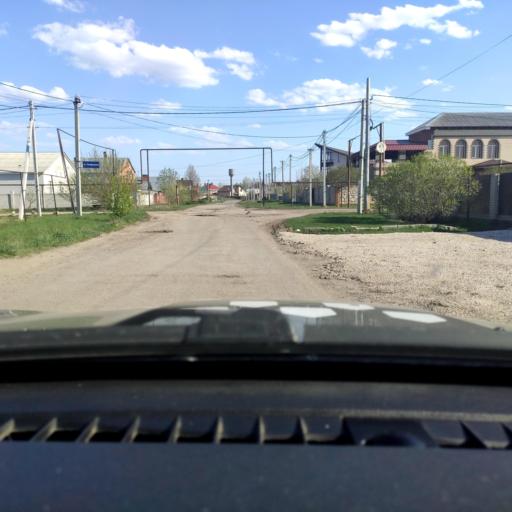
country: RU
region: Samara
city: Tol'yatti
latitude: 53.5672
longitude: 49.3791
